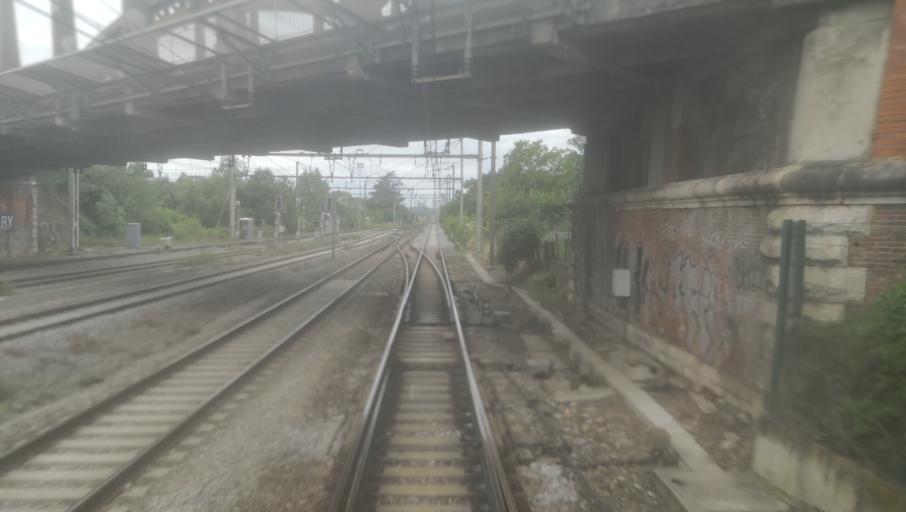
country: FR
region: Languedoc-Roussillon
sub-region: Departement de l'Aude
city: Castelnaudary
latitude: 43.3125
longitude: 1.9464
